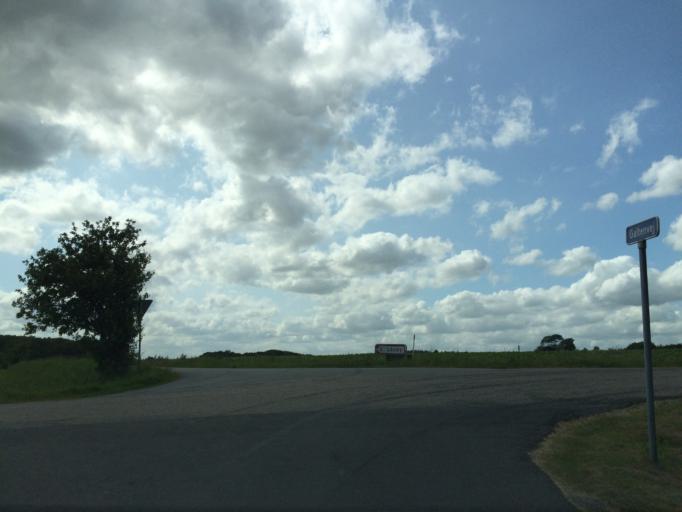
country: DK
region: Central Jutland
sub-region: Skanderborg Kommune
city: Galten
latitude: 56.1649
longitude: 9.8405
